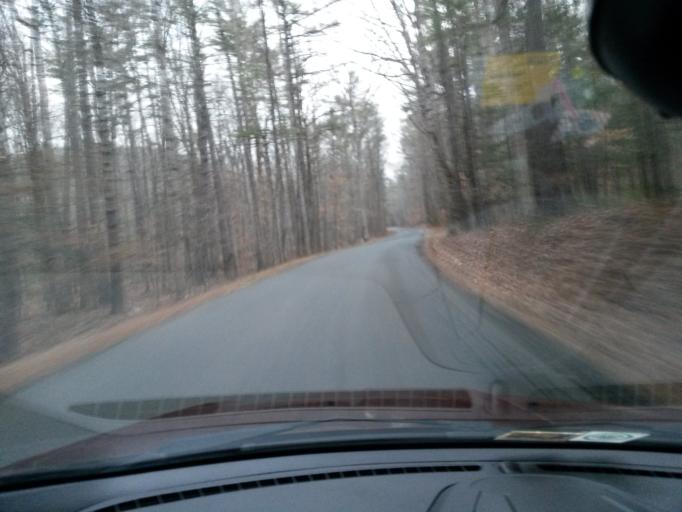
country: US
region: Virginia
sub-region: Alleghany County
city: Clifton Forge
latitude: 37.9209
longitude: -79.7929
